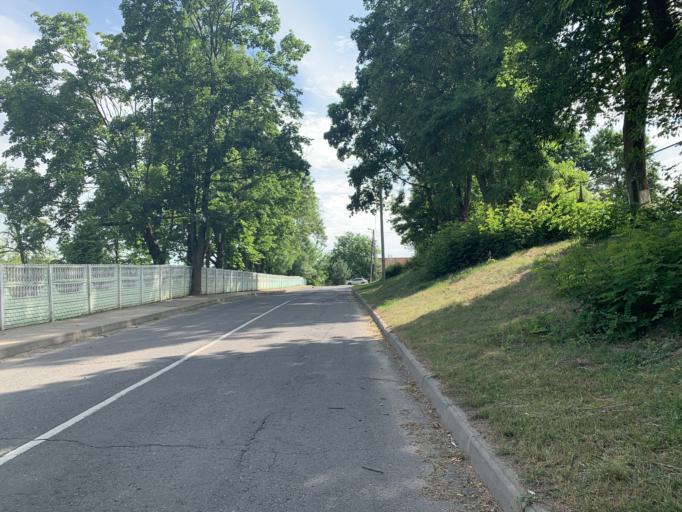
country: BY
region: Minsk
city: Nyasvizh
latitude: 53.2147
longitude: 26.6818
